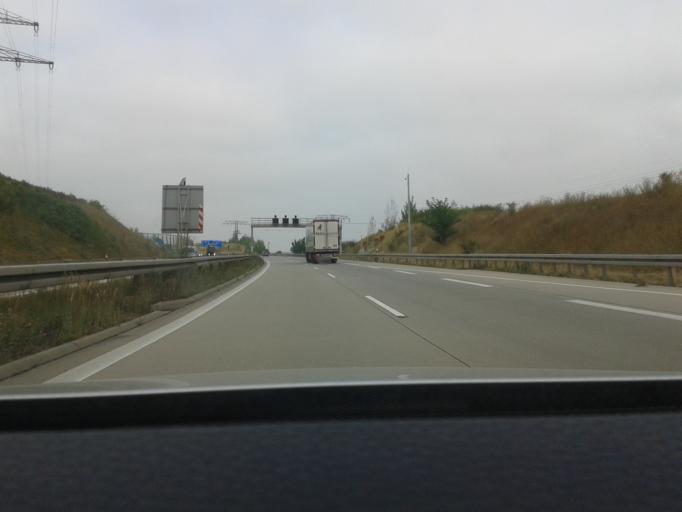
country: DE
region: Saxony
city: Bannewitz
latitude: 51.0045
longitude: 13.7413
